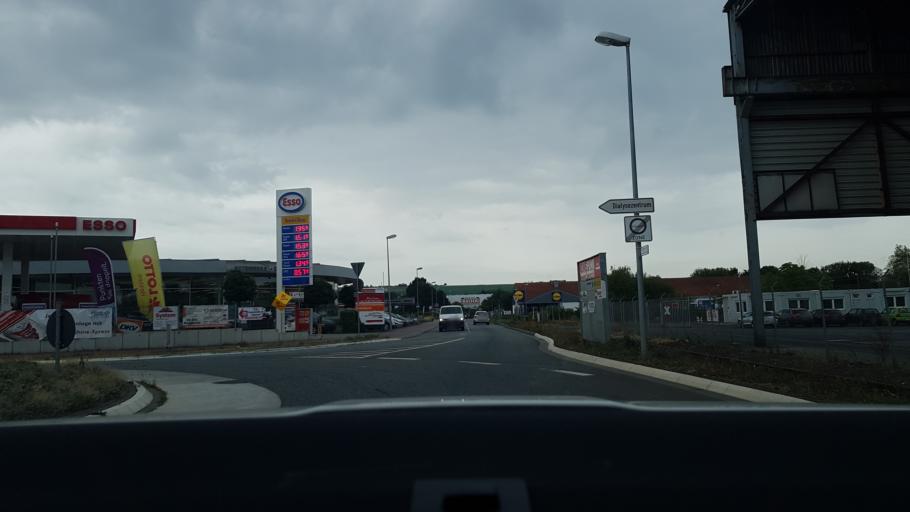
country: DE
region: Hesse
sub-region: Regierungsbezirk Giessen
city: Limburg an der Lahn
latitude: 50.3768
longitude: 8.0541
